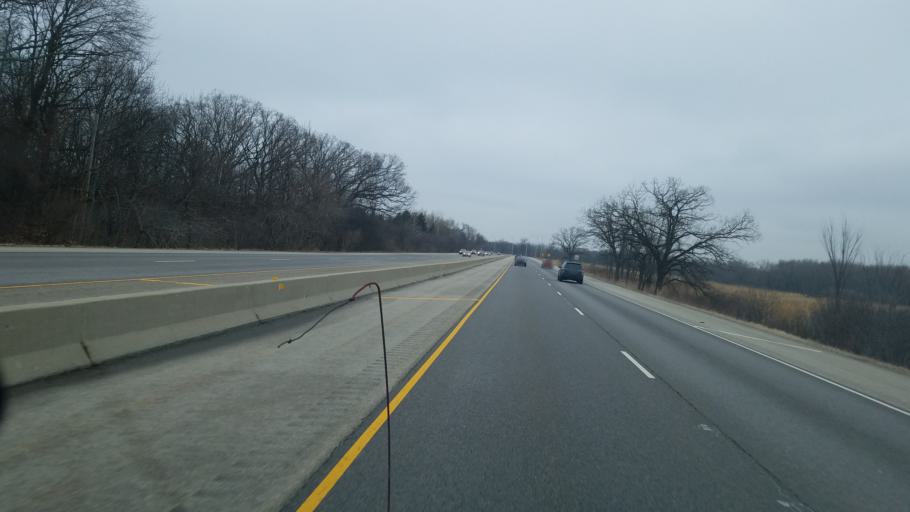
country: US
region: Illinois
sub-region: Lake County
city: Wadsworth
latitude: 42.4381
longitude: -87.9380
